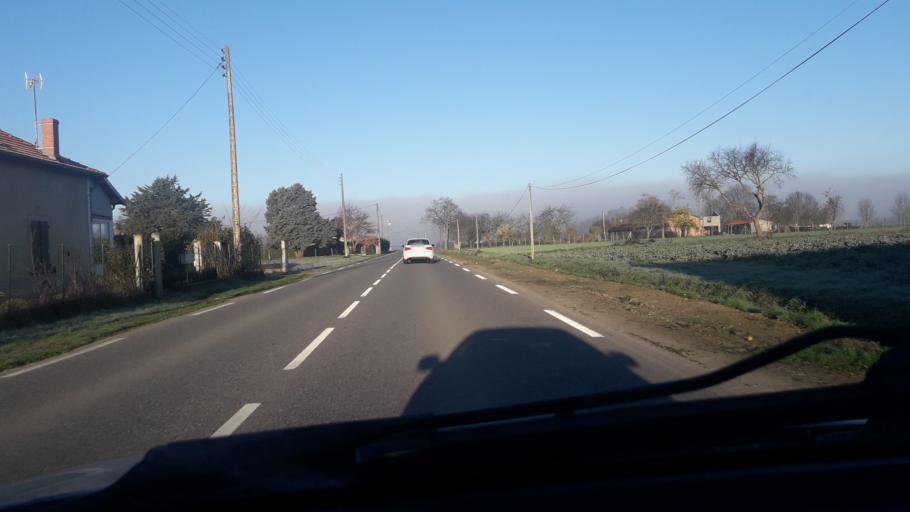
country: FR
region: Midi-Pyrenees
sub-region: Departement de la Haute-Garonne
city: Carbonne
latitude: 43.2981
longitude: 1.1961
